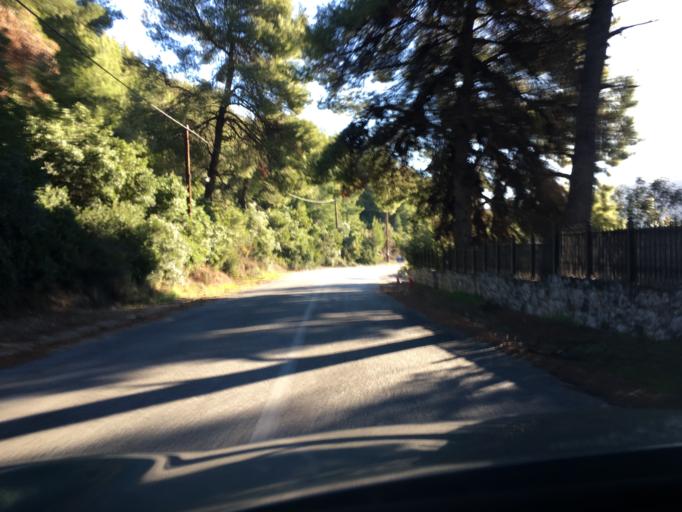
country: GR
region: Thessaly
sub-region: Nomos Magnisias
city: Skopelos
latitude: 39.1138
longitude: 23.6554
